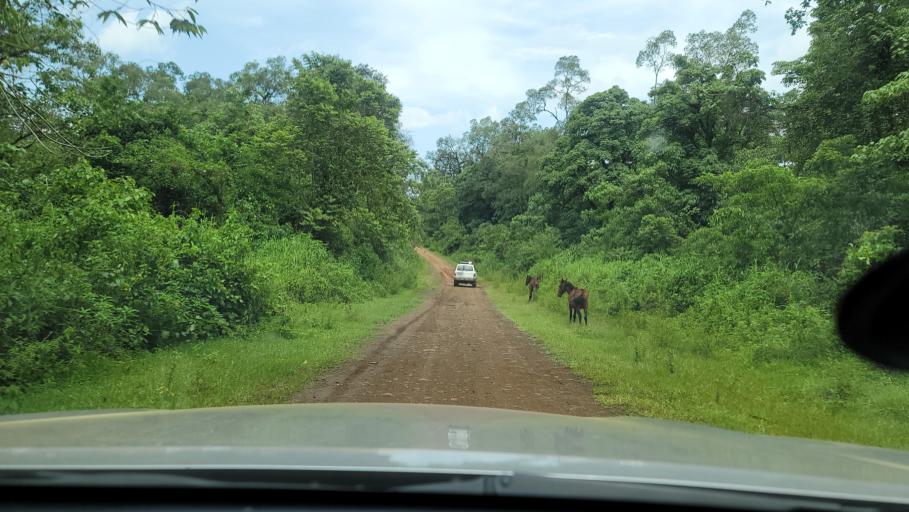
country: ET
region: Southern Nations, Nationalities, and People's Region
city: Bonga
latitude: 7.6464
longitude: 36.2447
